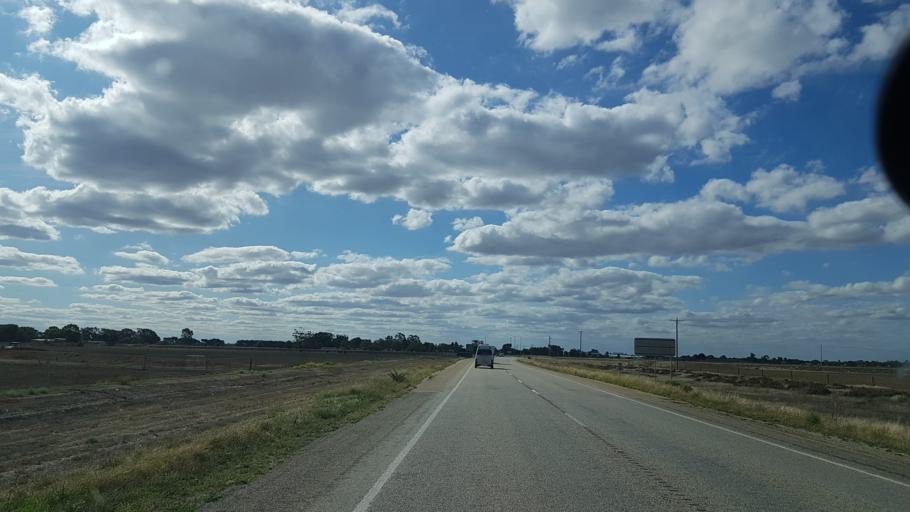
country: AU
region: Victoria
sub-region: Swan Hill
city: Swan Hill
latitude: -35.7669
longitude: 143.9330
